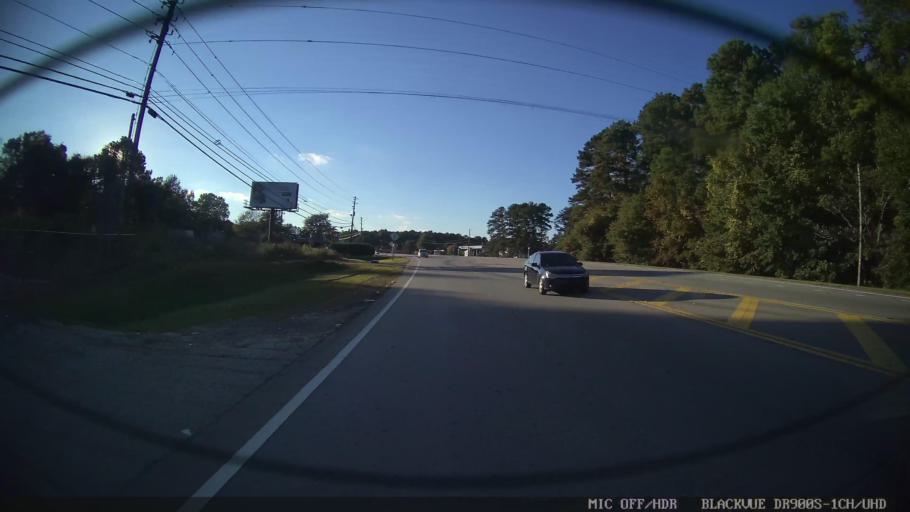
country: US
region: Georgia
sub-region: Henry County
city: Stockbridge
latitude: 33.5777
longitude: -84.2716
